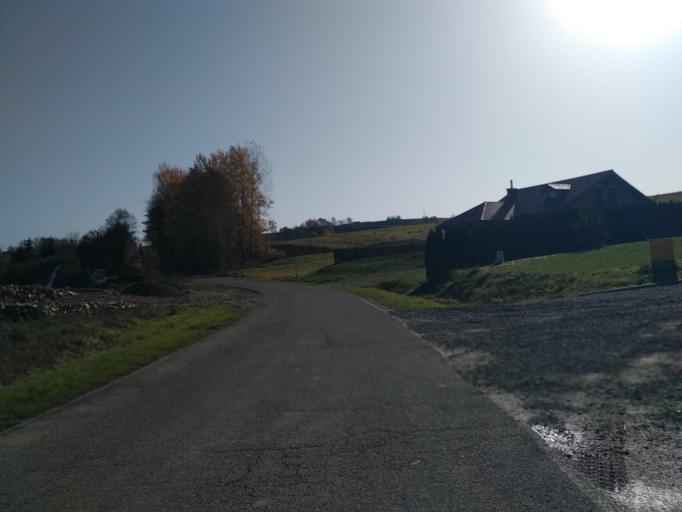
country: PL
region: Subcarpathian Voivodeship
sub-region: Powiat rzeszowski
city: Blazowa
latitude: 49.8735
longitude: 22.1156
